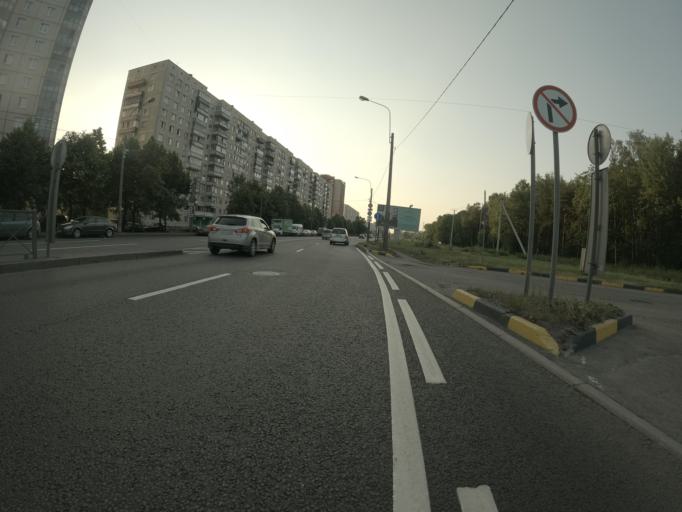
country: RU
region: St.-Petersburg
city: Krasnogvargeisky
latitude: 59.9468
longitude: 30.5047
